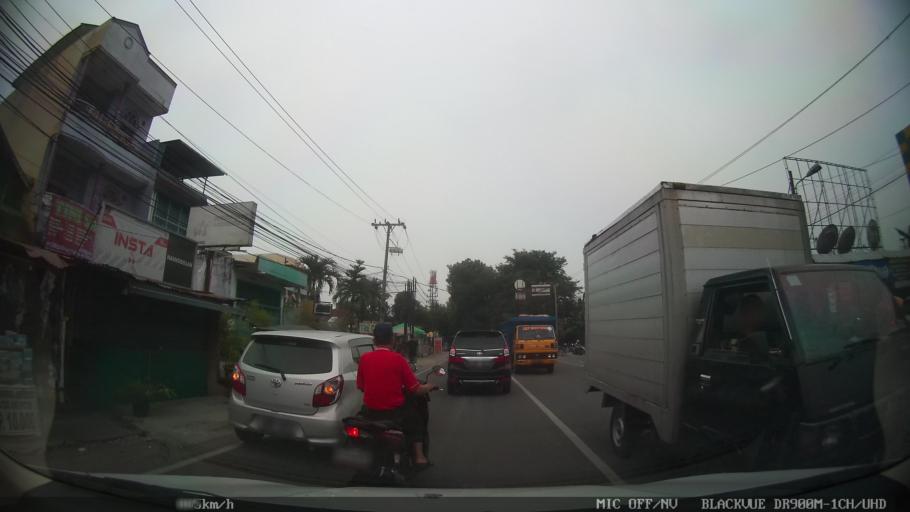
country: ID
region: North Sumatra
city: Medan
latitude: 3.5684
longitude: 98.7031
